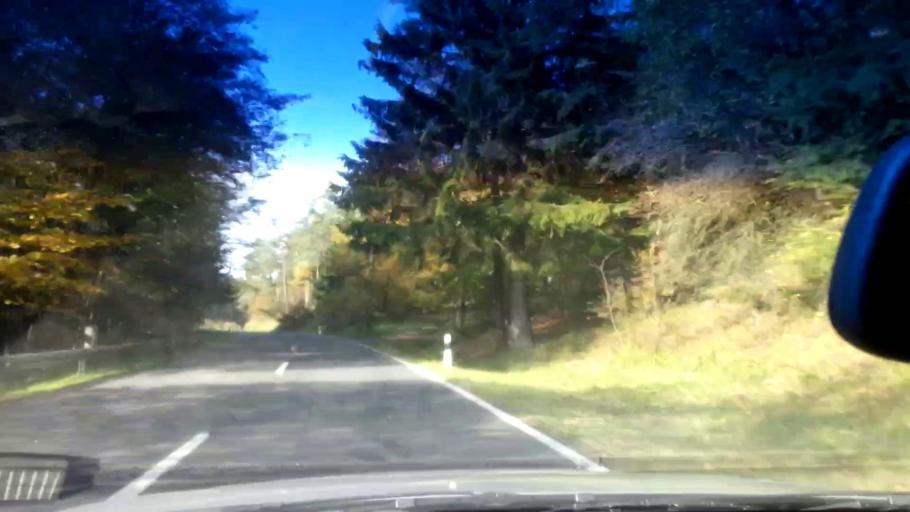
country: DE
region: Bavaria
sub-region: Upper Franconia
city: Stadelhofen
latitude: 49.9581
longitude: 11.2116
